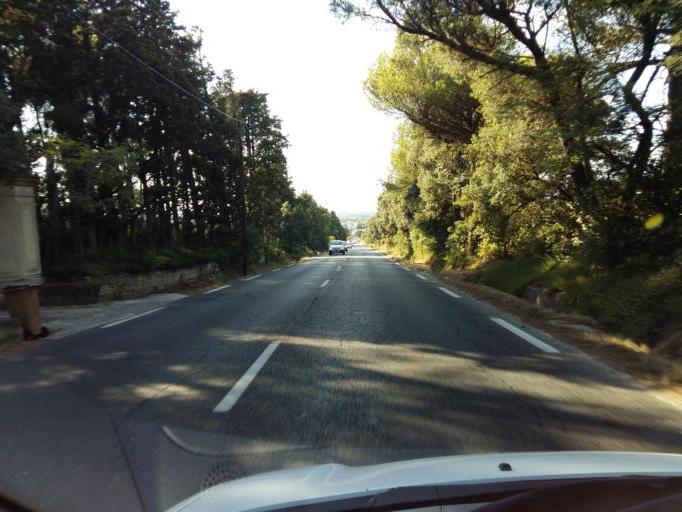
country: FR
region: Provence-Alpes-Cote d'Azur
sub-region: Departement du Vaucluse
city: Jonquerettes
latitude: 43.9359
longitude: 4.9188
